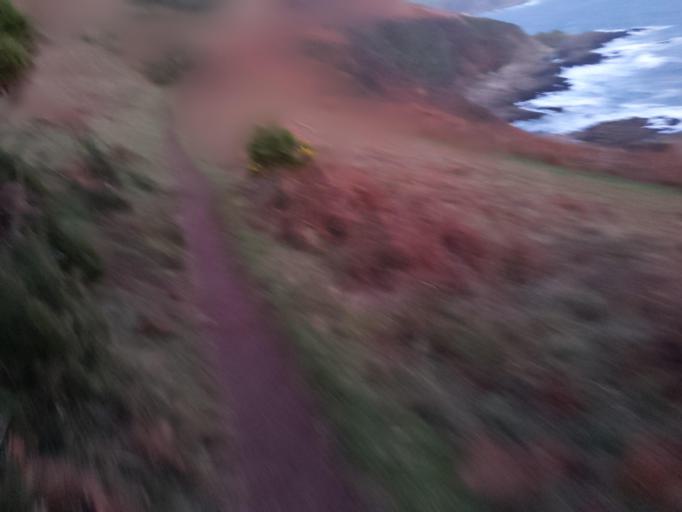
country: GB
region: England
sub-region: Cornwall
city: Fowey
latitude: 50.3273
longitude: -4.5968
